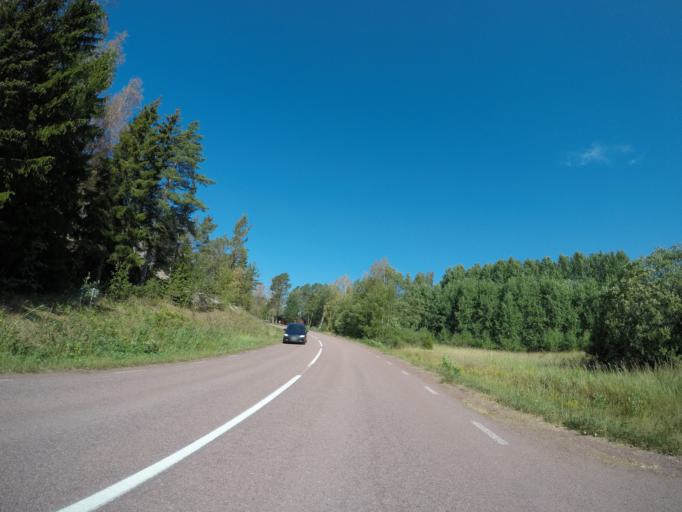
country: AX
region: Alands landsbygd
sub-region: Finstroem
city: Finstroem
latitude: 60.2740
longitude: 19.9199
